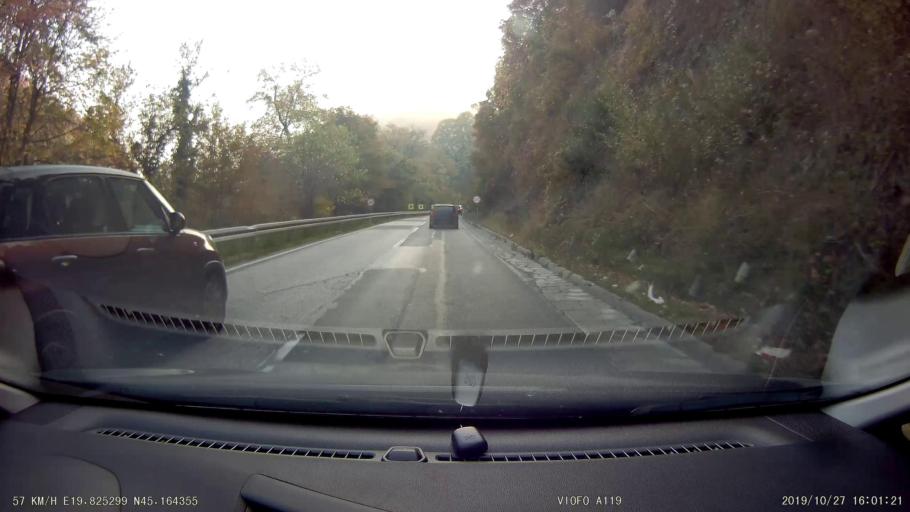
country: RS
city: Vrdnik
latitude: 45.1642
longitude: 19.8253
